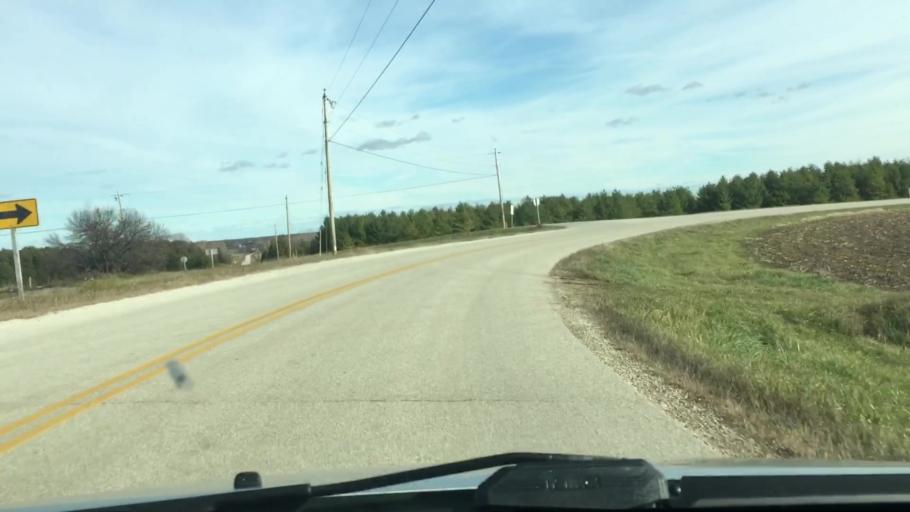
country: US
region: Wisconsin
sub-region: Kewaunee County
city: Algoma
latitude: 44.6974
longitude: -87.5813
